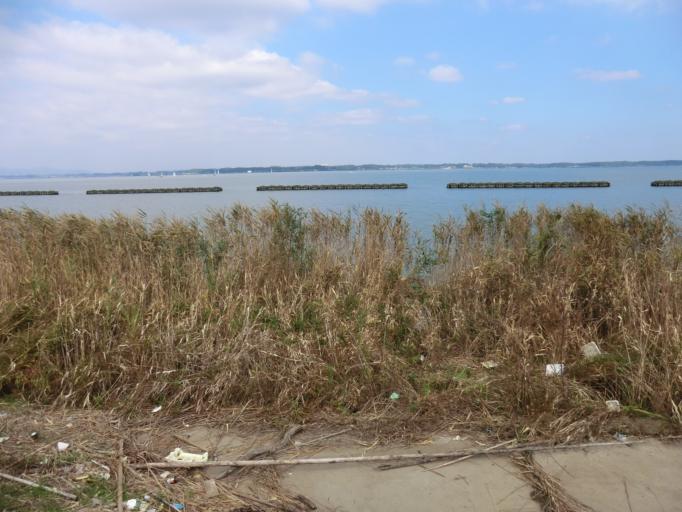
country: JP
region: Ibaraki
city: Ami
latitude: 36.0400
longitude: 140.2450
